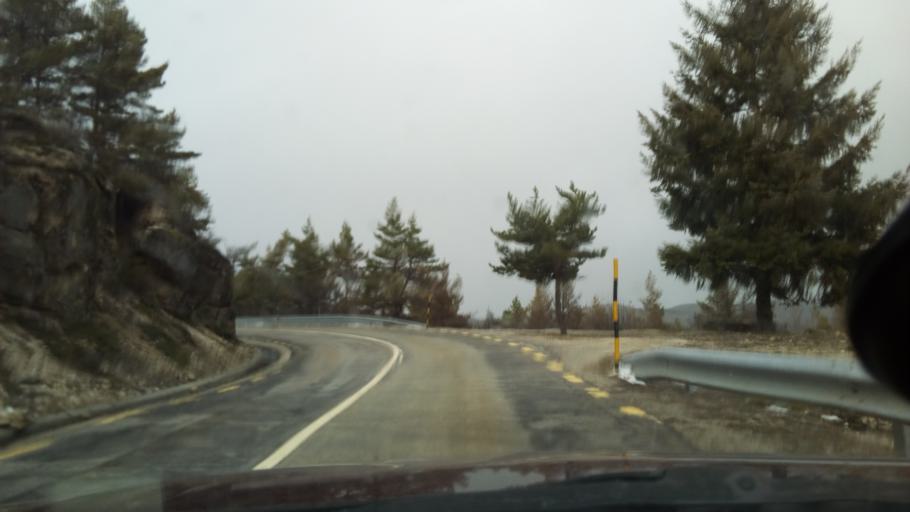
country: PT
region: Guarda
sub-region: Manteigas
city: Manteigas
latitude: 40.4121
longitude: -7.5721
